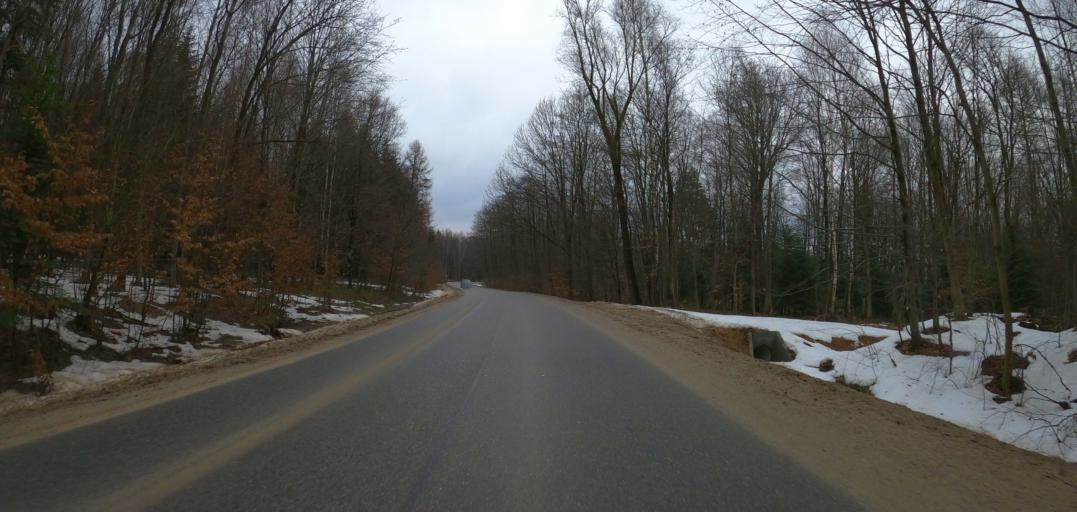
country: PL
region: Subcarpathian Voivodeship
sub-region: Powiat debicki
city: Debica
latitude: 49.9825
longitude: 21.4100
